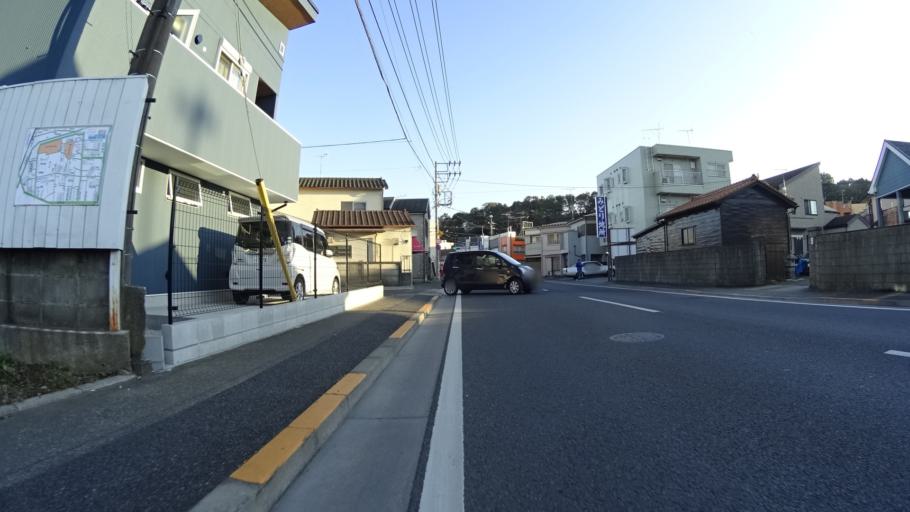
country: JP
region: Tokyo
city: Hachioji
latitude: 35.6650
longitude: 139.3044
